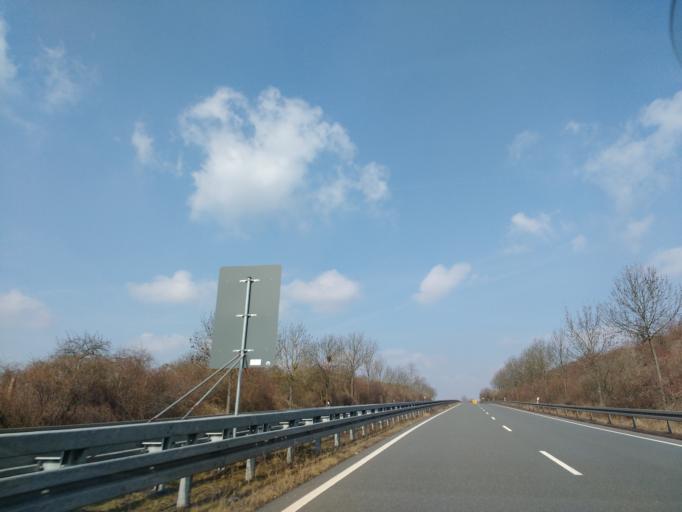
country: DE
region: Saxony-Anhalt
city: Roblingen am See
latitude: 51.4802
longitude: 11.7085
